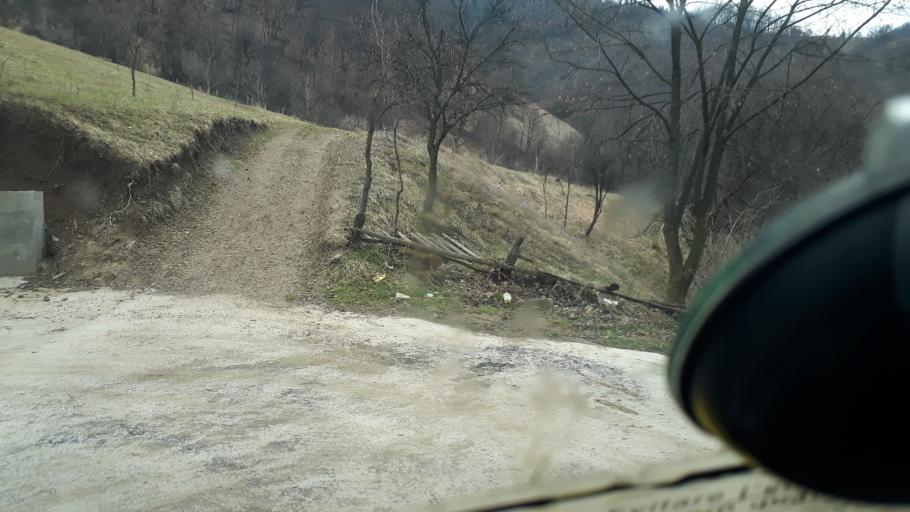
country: BA
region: Federation of Bosnia and Herzegovina
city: Zenica
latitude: 44.1487
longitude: 17.9667
